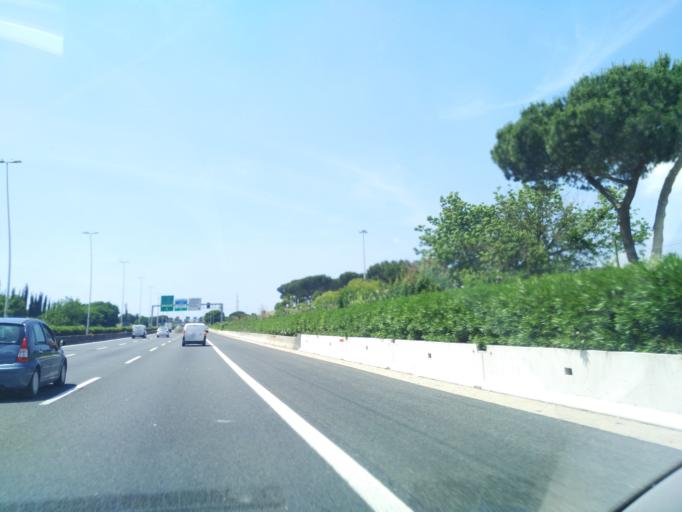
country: IT
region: Latium
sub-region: Citta metropolitana di Roma Capitale
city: Selcetta
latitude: 41.7966
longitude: 12.4901
